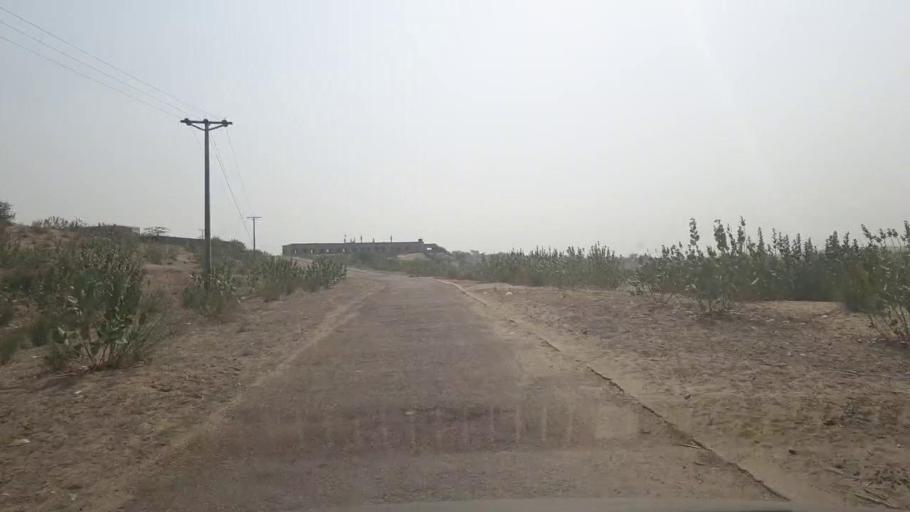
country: PK
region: Sindh
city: Chor
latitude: 25.5924
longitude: 69.9893
